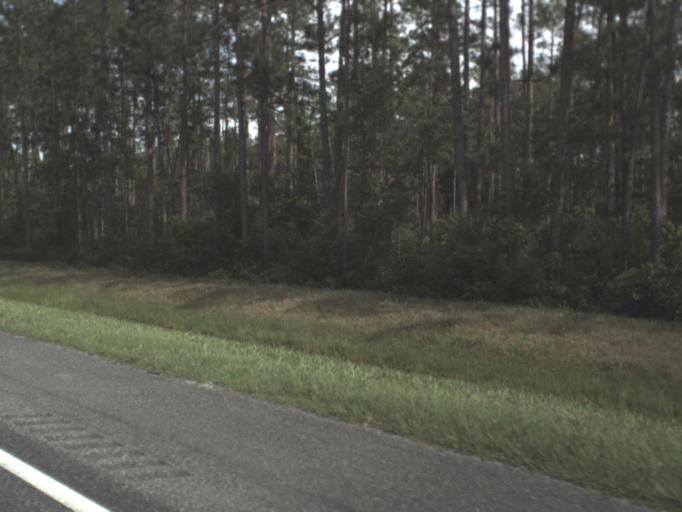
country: US
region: Florida
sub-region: Baker County
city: Macclenny
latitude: 30.2541
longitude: -82.3478
